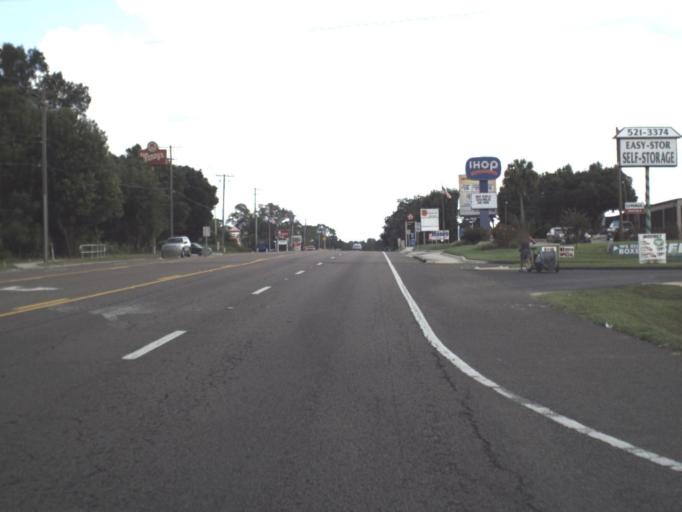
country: US
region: Florida
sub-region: Pasco County
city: Dade City
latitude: 28.3482
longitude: -82.1874
